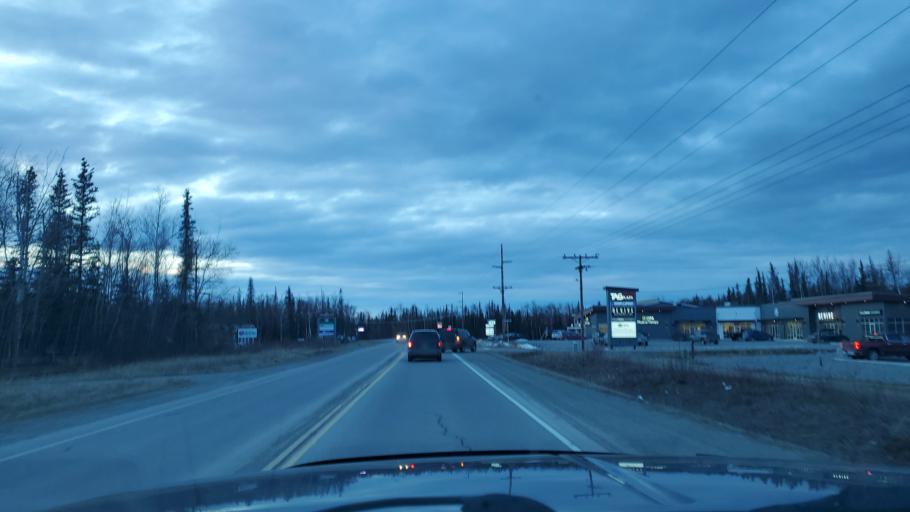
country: US
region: Alaska
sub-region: Matanuska-Susitna Borough
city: Wasilla
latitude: 61.5889
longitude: -149.4093
